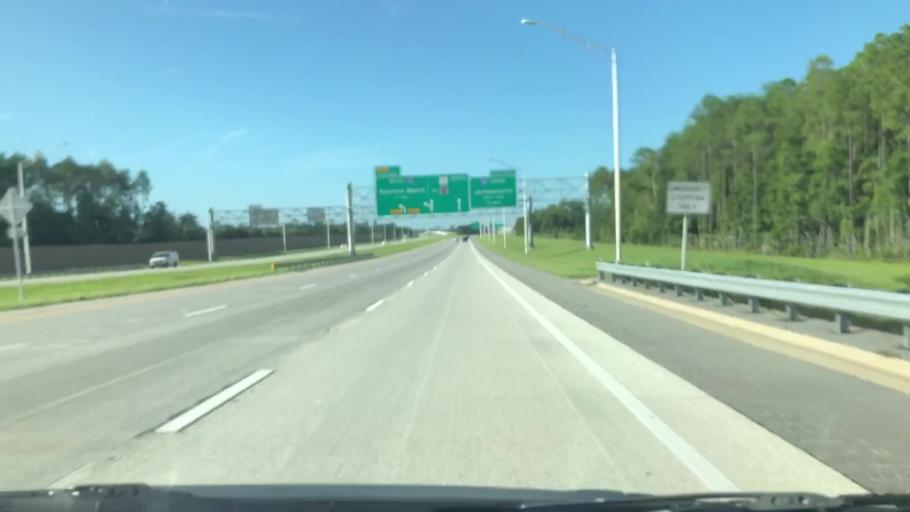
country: US
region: Florida
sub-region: Saint Johns County
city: Palm Valley
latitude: 30.1302
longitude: -81.5106
